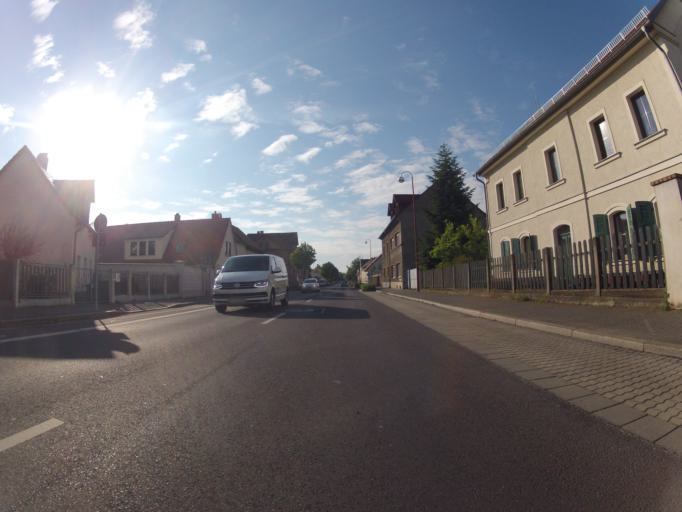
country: DE
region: Saxony
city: Grossposna
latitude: 51.2805
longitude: 12.4637
